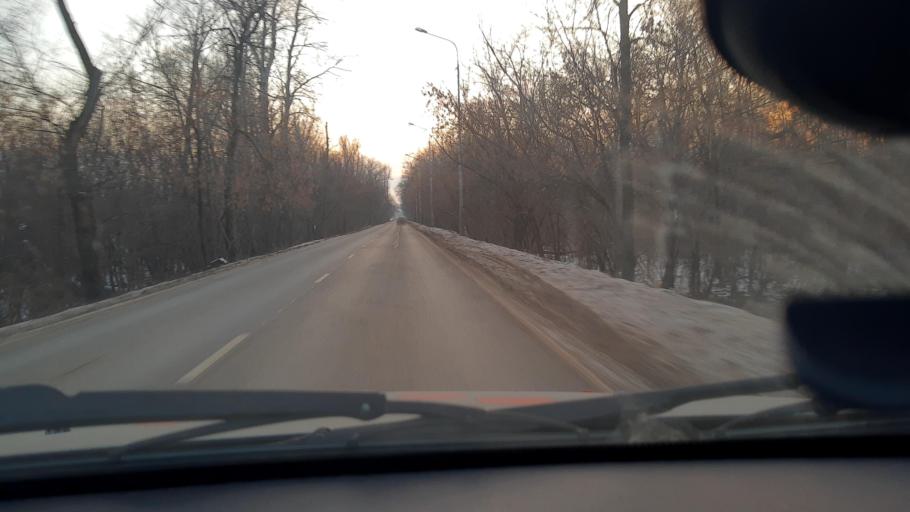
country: RU
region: Bashkortostan
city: Ufa
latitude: 54.6633
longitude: 55.9377
